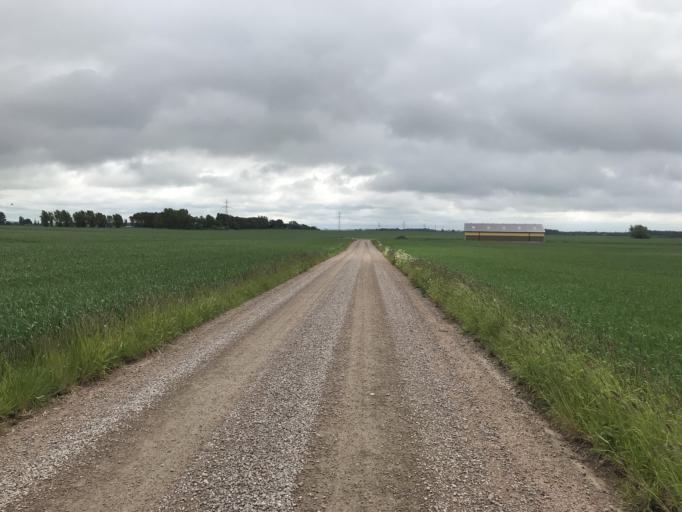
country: SE
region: Skane
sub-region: Landskrona
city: Asmundtorp
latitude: 55.8719
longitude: 12.8929
